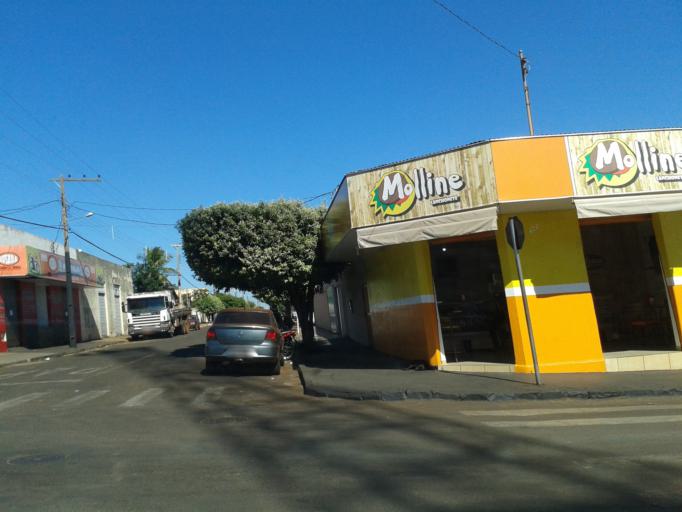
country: BR
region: Minas Gerais
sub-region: Santa Vitoria
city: Santa Vitoria
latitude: -18.8404
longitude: -50.1239
